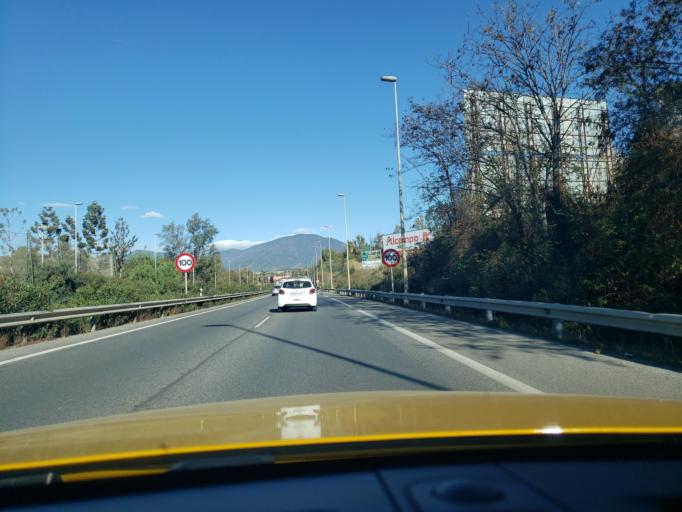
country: ES
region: Andalusia
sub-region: Provincia de Malaga
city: Marbella
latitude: 36.5049
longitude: -4.9475
